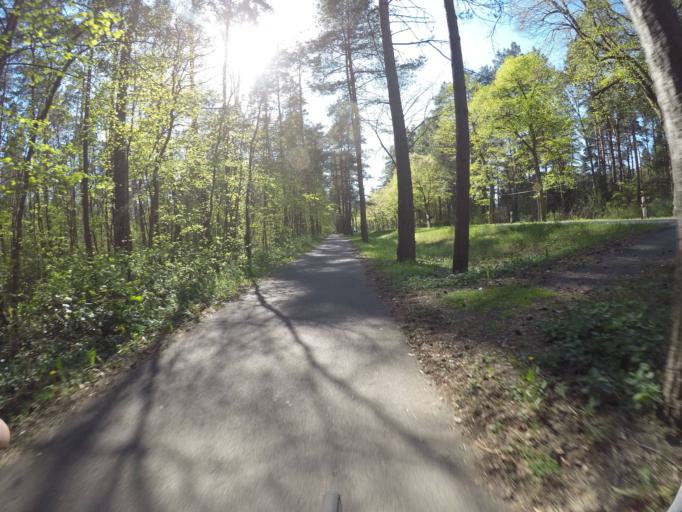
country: DE
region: Brandenburg
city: Rehfelde
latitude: 52.4546
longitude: 13.8920
